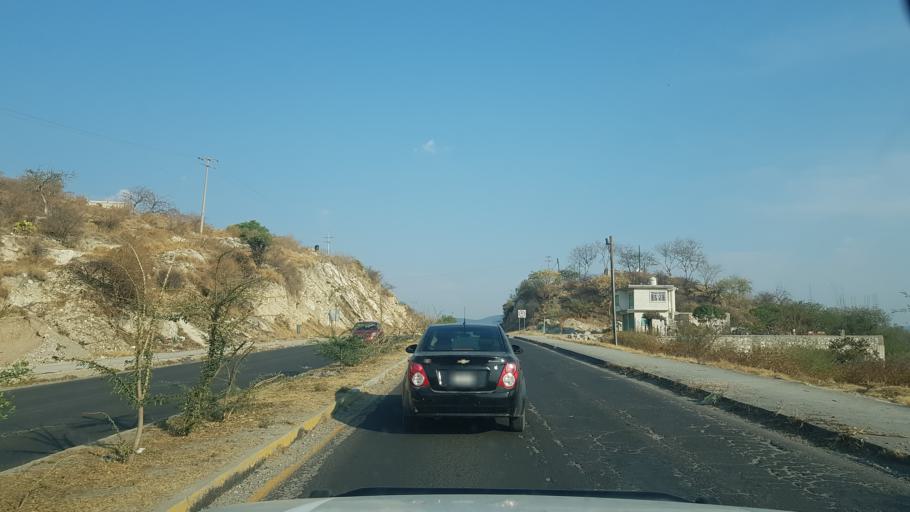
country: MX
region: Puebla
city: Izucar de Matamoros
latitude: 18.6046
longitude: -98.4845
